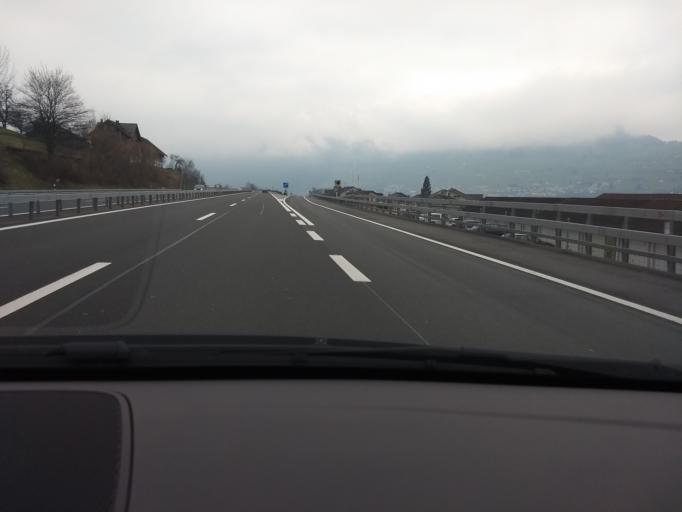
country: CH
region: Nidwalden
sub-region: Nidwalden
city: Buochs
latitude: 46.9715
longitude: 8.4450
